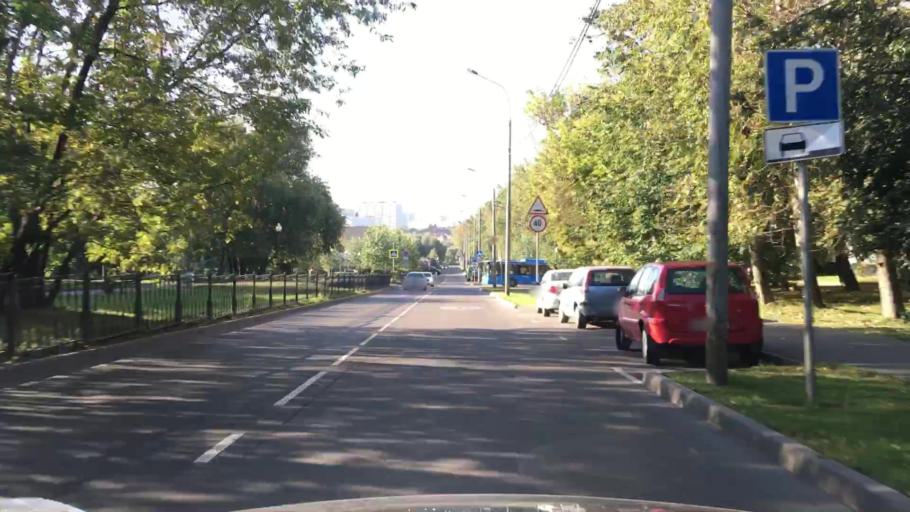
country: RU
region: Moscow
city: Davydkovo
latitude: 55.7180
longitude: 37.4618
